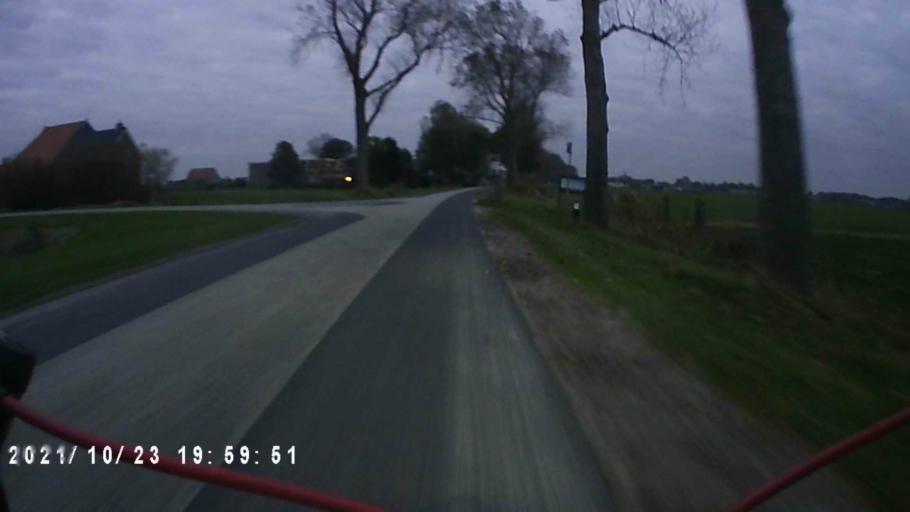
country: NL
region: Friesland
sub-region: Gemeente Harlingen
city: Harlingen
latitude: 53.1099
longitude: 5.4589
